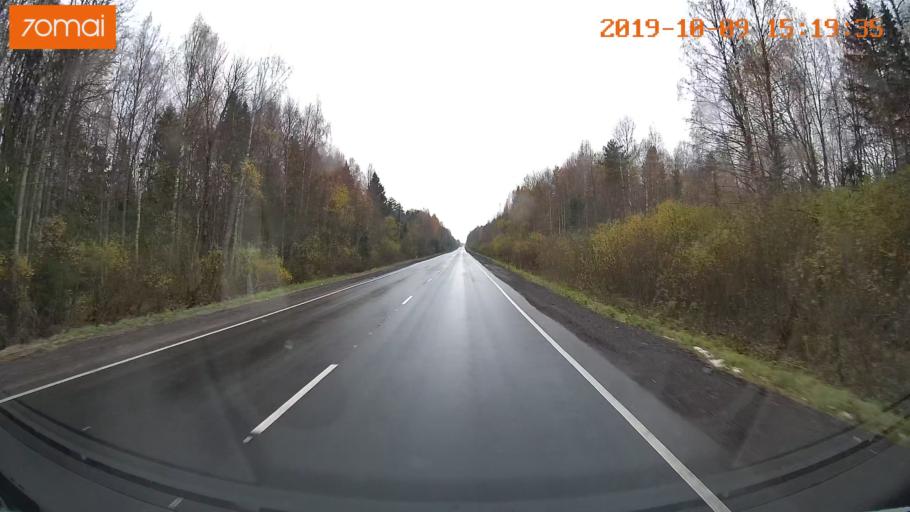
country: RU
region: Kostroma
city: Susanino
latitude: 58.0740
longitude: 41.5537
